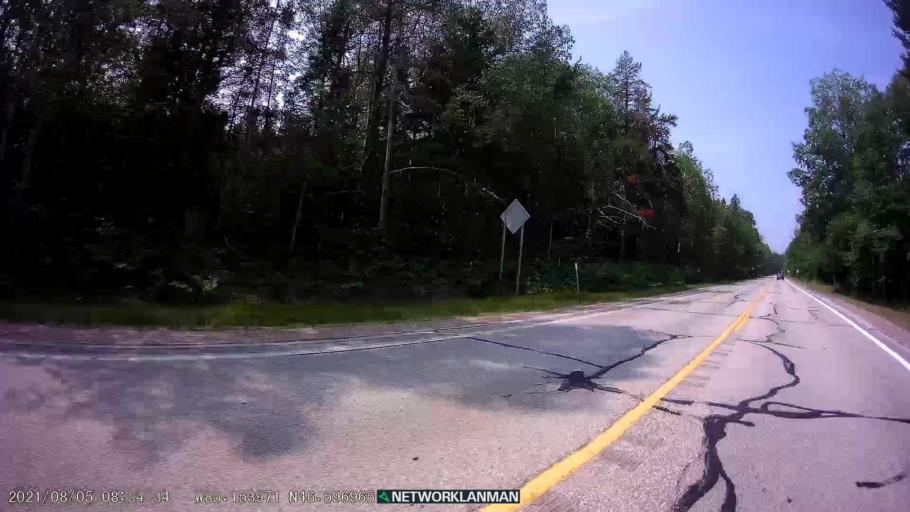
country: US
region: Michigan
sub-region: Luce County
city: Newberry
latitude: 46.5970
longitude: -85.1555
